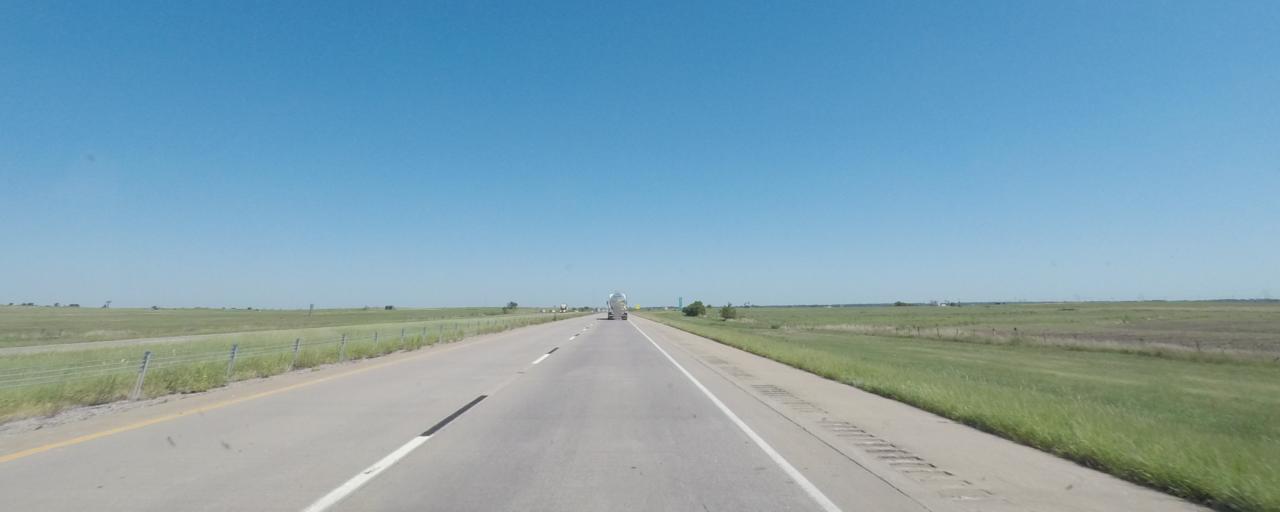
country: US
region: Oklahoma
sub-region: Kay County
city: Tonkawa
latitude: 36.6093
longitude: -97.3456
